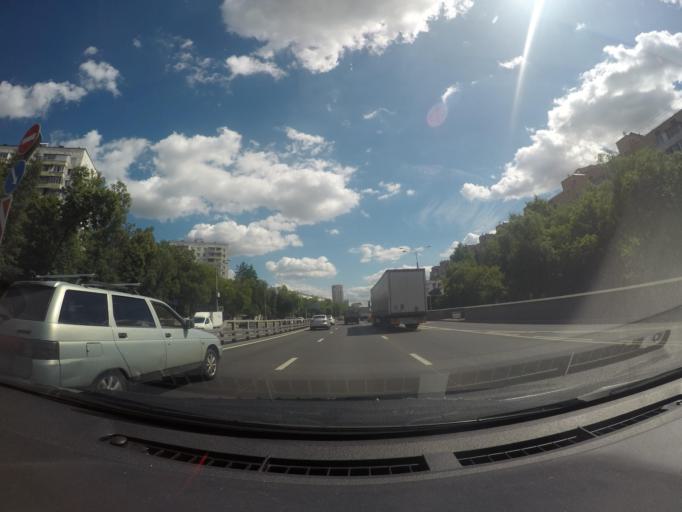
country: RU
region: Moscow
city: Novokuz'minki
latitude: 55.7164
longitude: 37.7985
